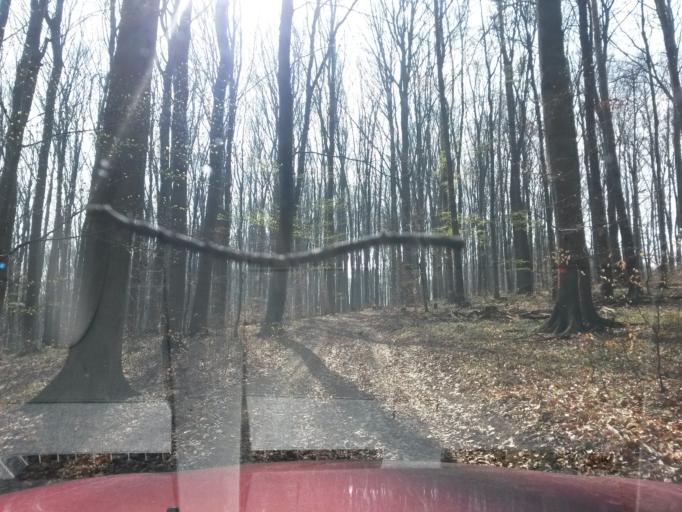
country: SK
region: Presovsky
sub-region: Okres Presov
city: Presov
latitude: 48.9317
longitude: 21.1527
